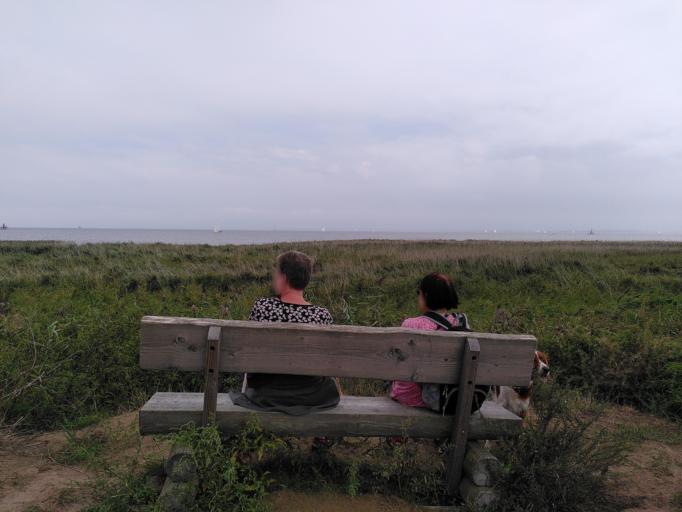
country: DE
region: Mecklenburg-Vorpommern
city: Ostseebad Dierhagen
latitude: 54.3494
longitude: 12.4193
